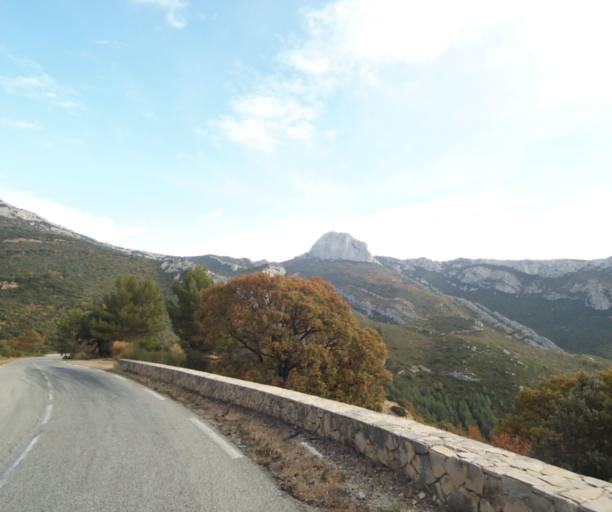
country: FR
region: Provence-Alpes-Cote d'Azur
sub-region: Departement des Bouches-du-Rhone
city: Gemenos
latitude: 43.3076
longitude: 5.6644
